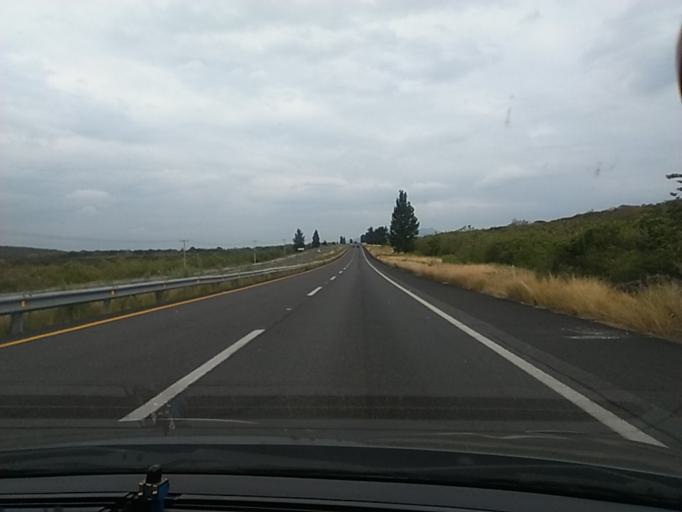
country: MX
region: Michoacan
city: Ecuandureo
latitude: 20.1698
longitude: -102.1450
